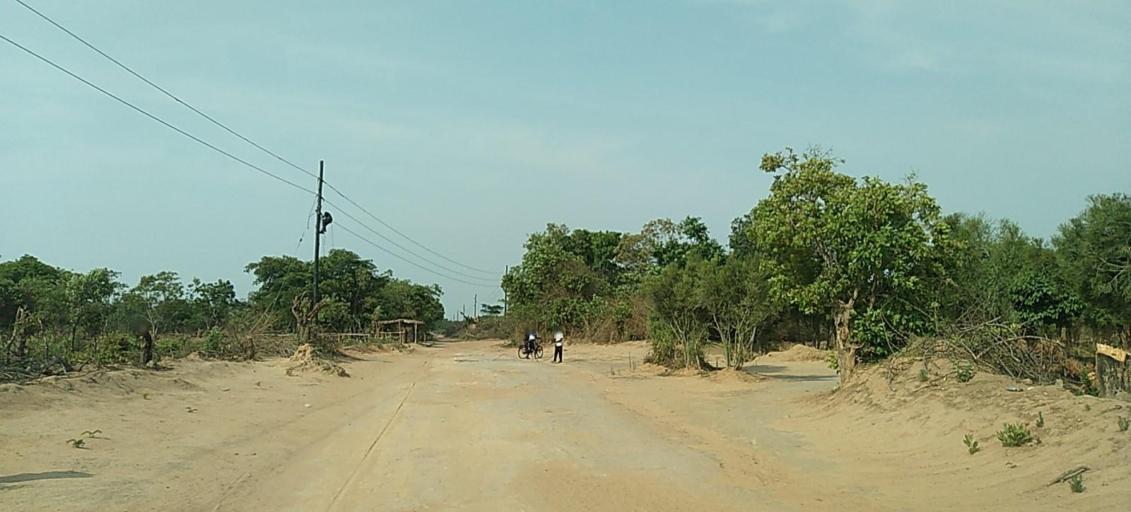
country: ZM
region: Copperbelt
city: Ndola
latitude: -13.2231
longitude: 28.6763
